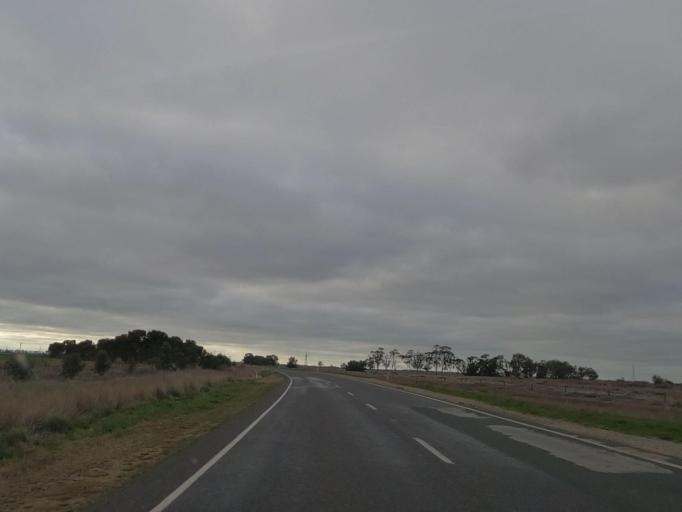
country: AU
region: Victoria
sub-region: Swan Hill
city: Swan Hill
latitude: -35.9199
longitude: 143.9416
